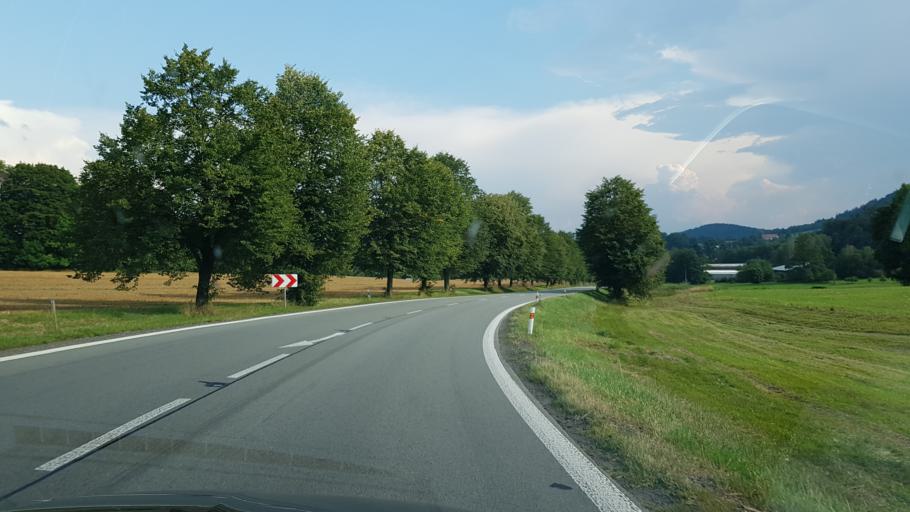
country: CZ
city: Vamberk
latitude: 50.1134
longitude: 16.3614
